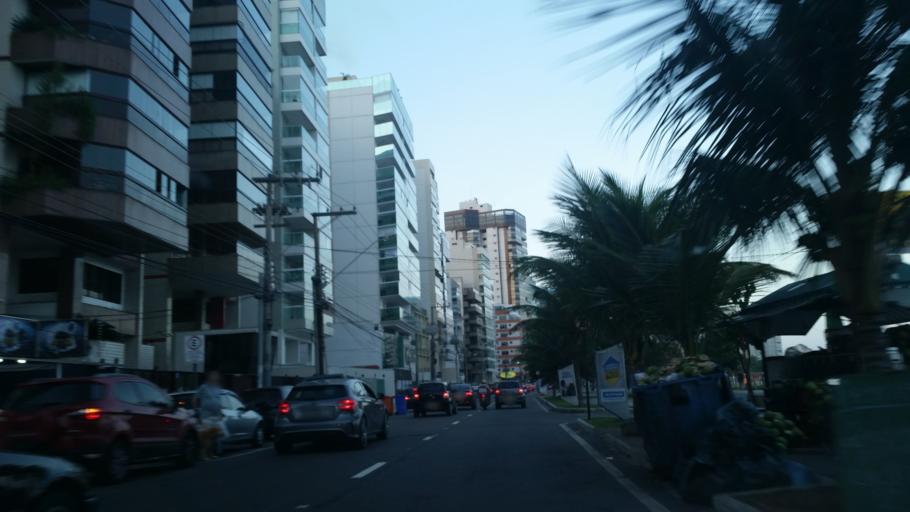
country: BR
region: Espirito Santo
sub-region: Vila Velha
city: Vila Velha
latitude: -20.3343
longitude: -40.2799
